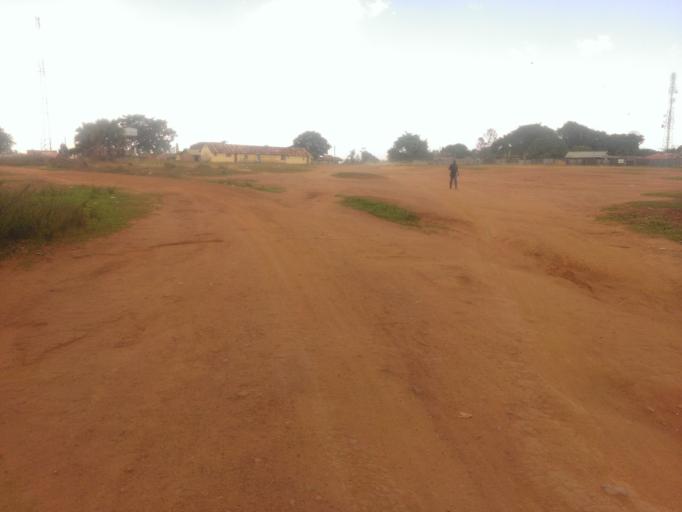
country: UG
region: Northern Region
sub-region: Gulu District
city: Gulu
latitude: 2.7803
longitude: 32.2965
